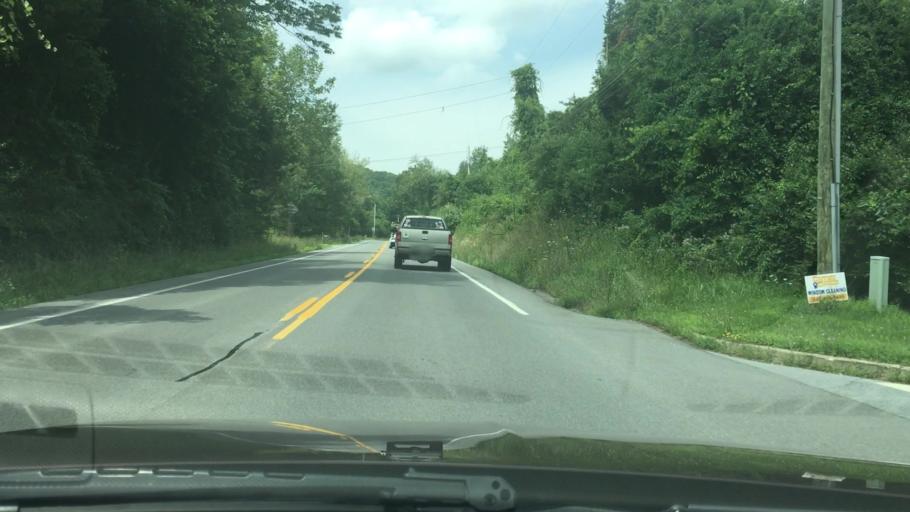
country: US
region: New York
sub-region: Dutchess County
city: Hillside Lake
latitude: 41.6297
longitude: -73.6995
